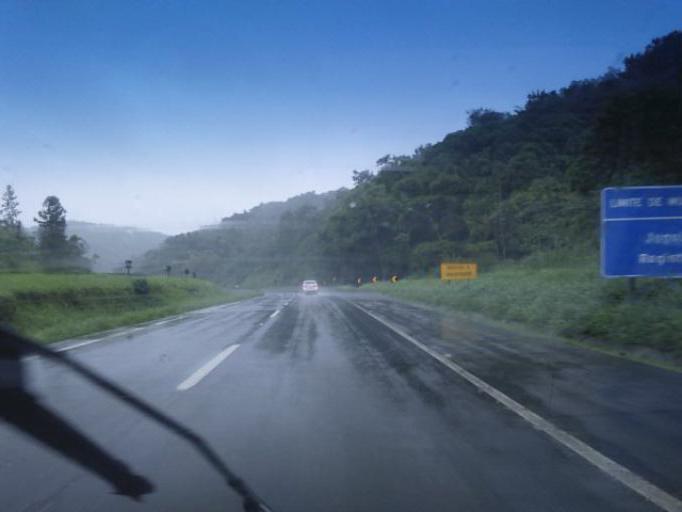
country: BR
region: Sao Paulo
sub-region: Juquia
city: Juquia
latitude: -24.3939
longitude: -47.7248
